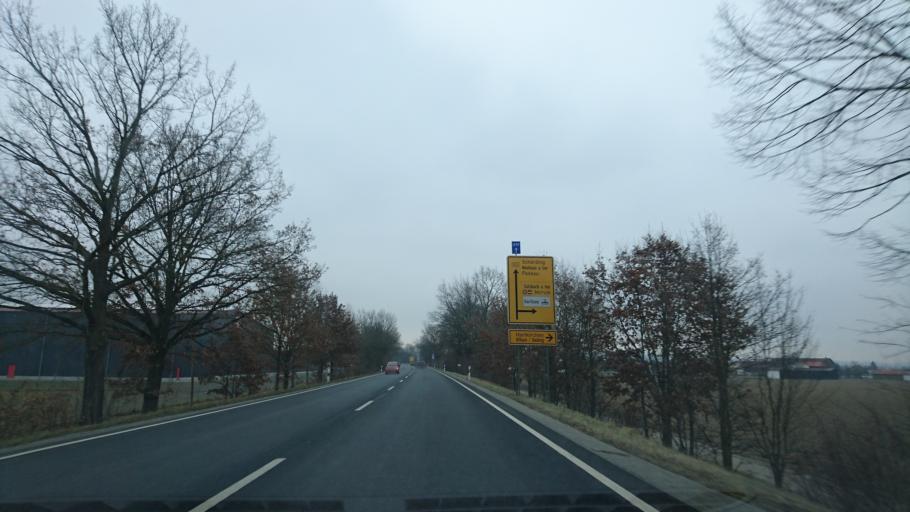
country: AT
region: Upper Austria
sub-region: Politischer Bezirk Scharding
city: Scharding
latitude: 48.4394
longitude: 13.3882
